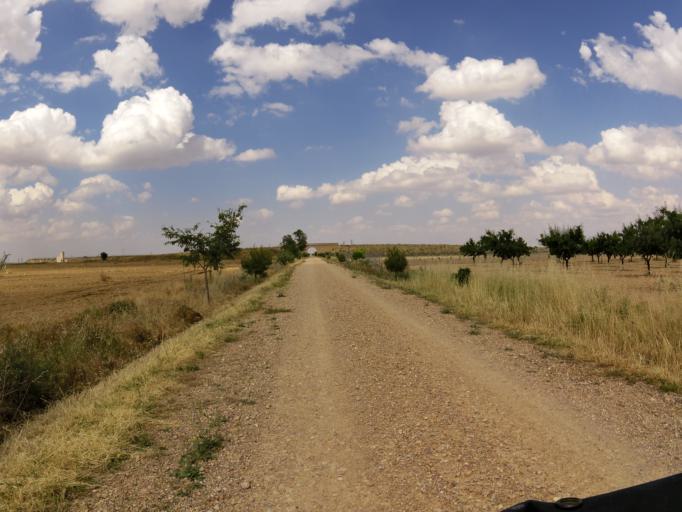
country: ES
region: Castille-La Mancha
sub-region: Provincia de Albacete
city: Albacete
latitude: 38.9293
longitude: -1.9954
